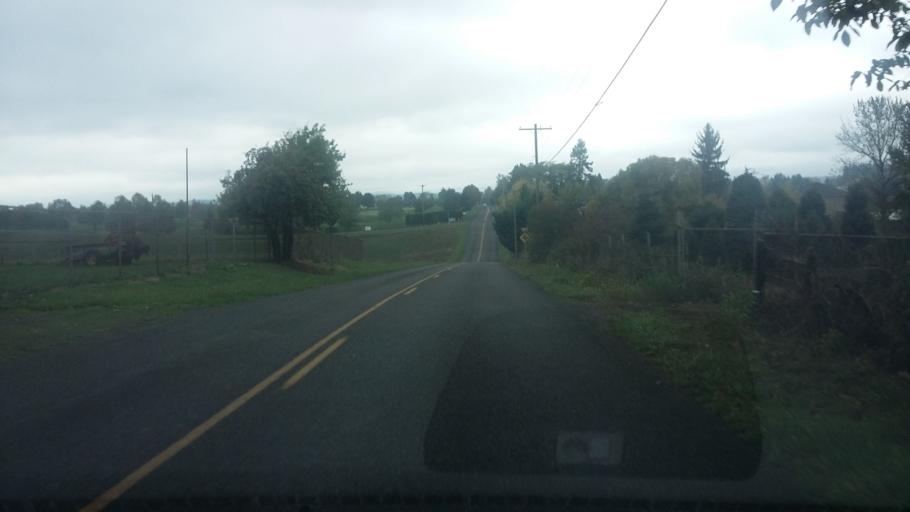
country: US
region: Washington
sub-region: Clark County
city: La Center
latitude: 45.8281
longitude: -122.6826
